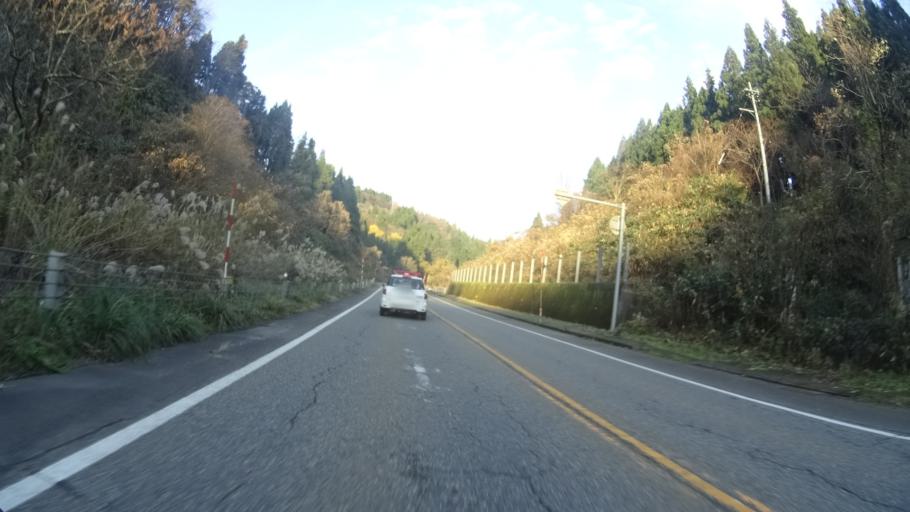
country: JP
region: Niigata
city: Kashiwazaki
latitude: 37.4056
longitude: 138.6935
